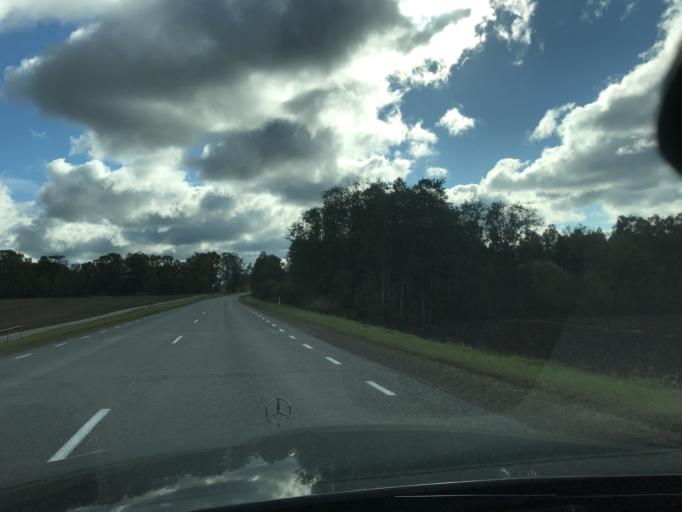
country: EE
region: Vorumaa
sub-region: Antsla vald
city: Vana-Antsla
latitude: 57.9423
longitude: 26.3049
